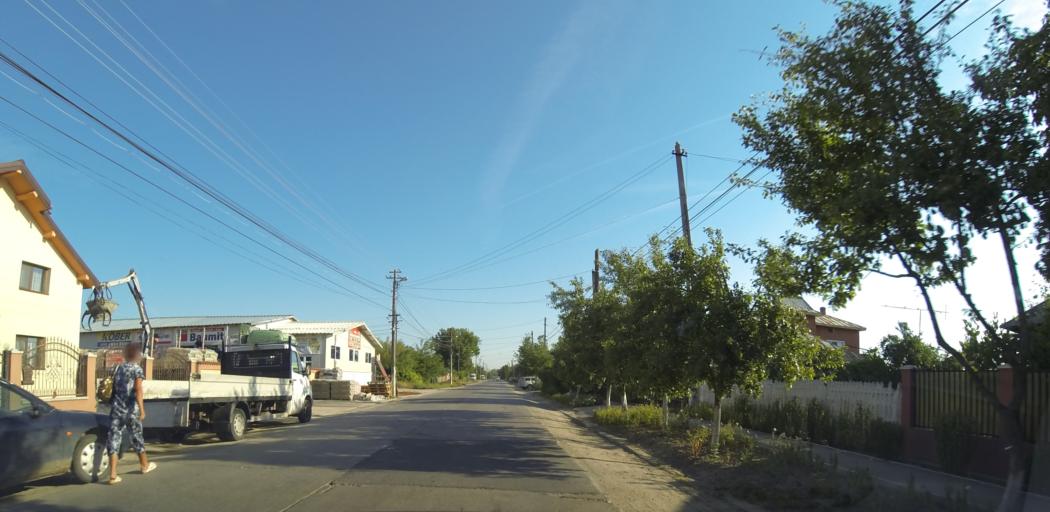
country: RO
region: Valcea
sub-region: Comuna Balcesti
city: Balcesti
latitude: 44.6232
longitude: 23.9420
